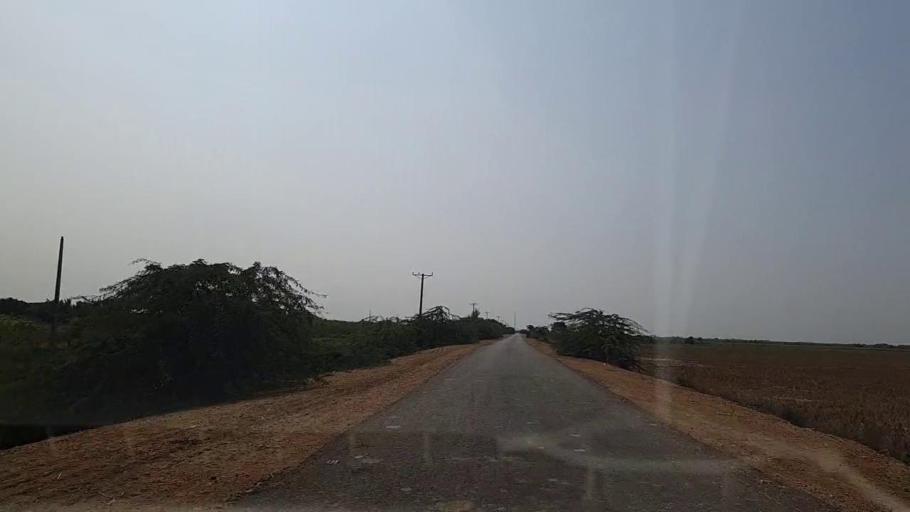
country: PK
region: Sindh
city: Chuhar Jamali
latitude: 24.2997
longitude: 67.9323
